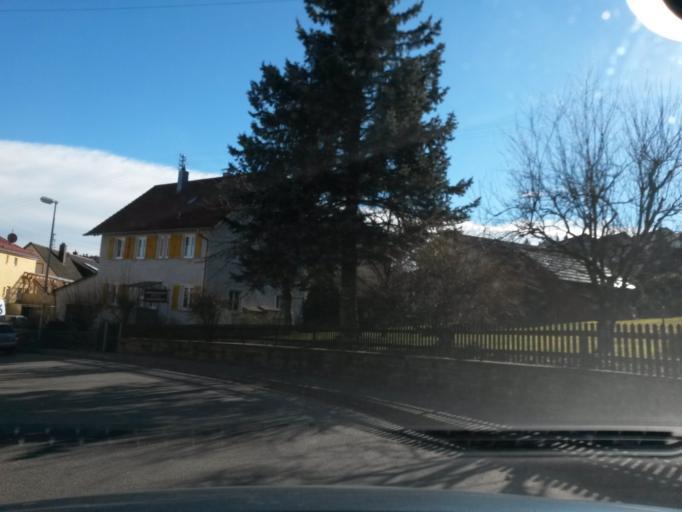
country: DE
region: Baden-Wuerttemberg
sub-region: Karlsruhe Region
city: Schomberg
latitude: 48.7875
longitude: 8.6413
